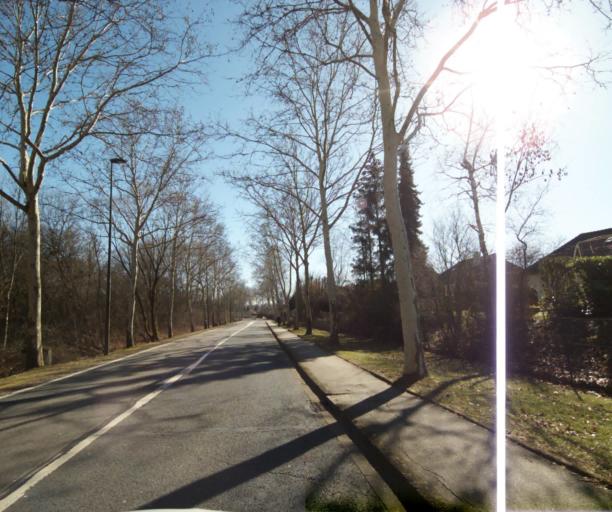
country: FR
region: Lorraine
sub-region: Departement de Meurthe-et-Moselle
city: Heillecourt
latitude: 48.6544
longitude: 6.2020
